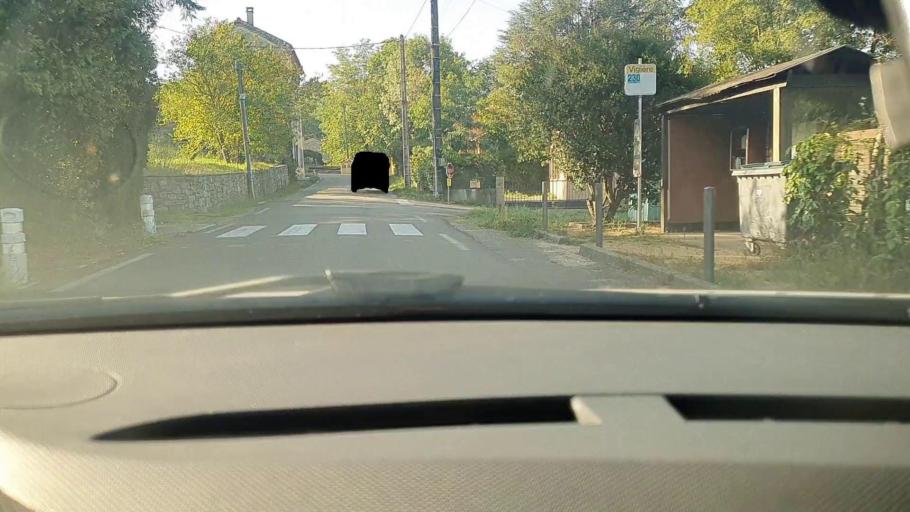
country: FR
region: Languedoc-Roussillon
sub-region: Departement du Gard
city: Besseges
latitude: 44.3126
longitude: 4.1301
